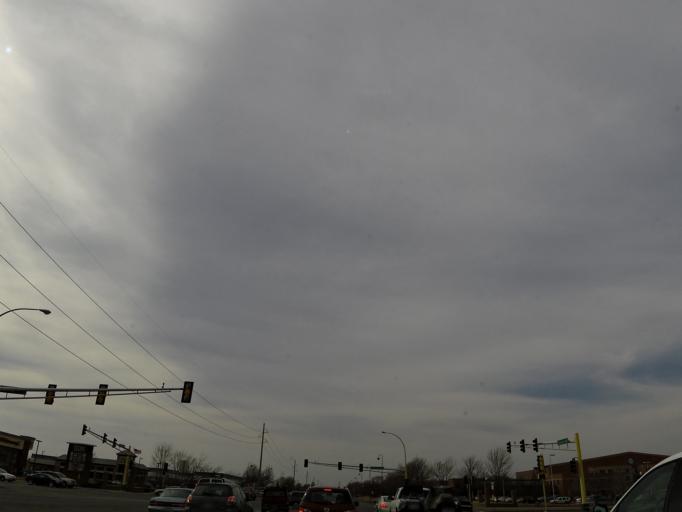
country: US
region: Minnesota
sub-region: Dakota County
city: Apple Valley
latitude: 44.7320
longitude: -93.2070
